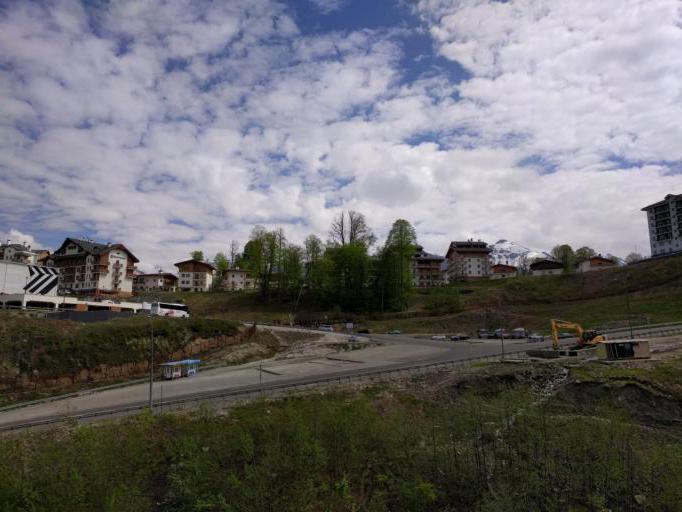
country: RU
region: Krasnodarskiy
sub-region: Sochi City
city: Krasnaya Polyana
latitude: 43.6614
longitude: 40.3146
